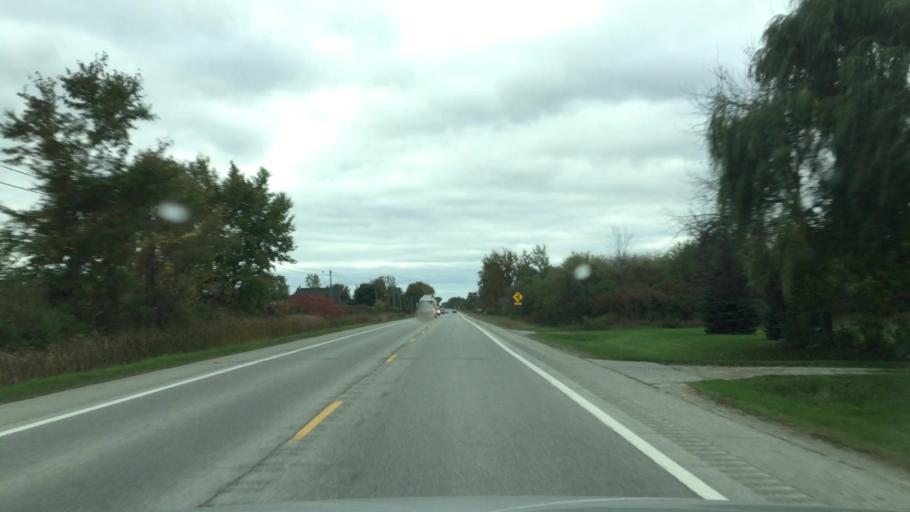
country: US
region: Michigan
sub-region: Macomb County
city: Memphis
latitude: 42.9653
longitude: -82.7637
